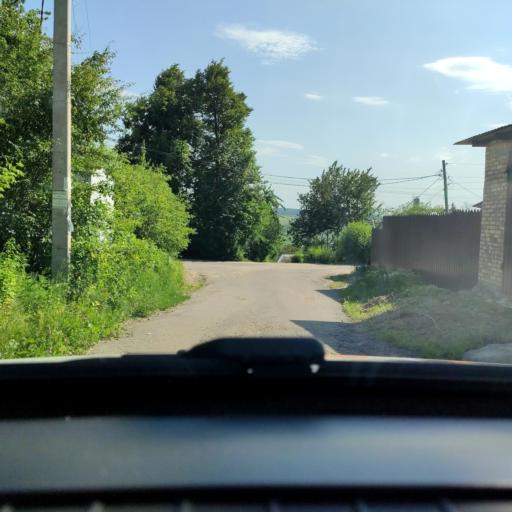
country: RU
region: Voronezj
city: Semiluki
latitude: 51.6905
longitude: 39.0105
